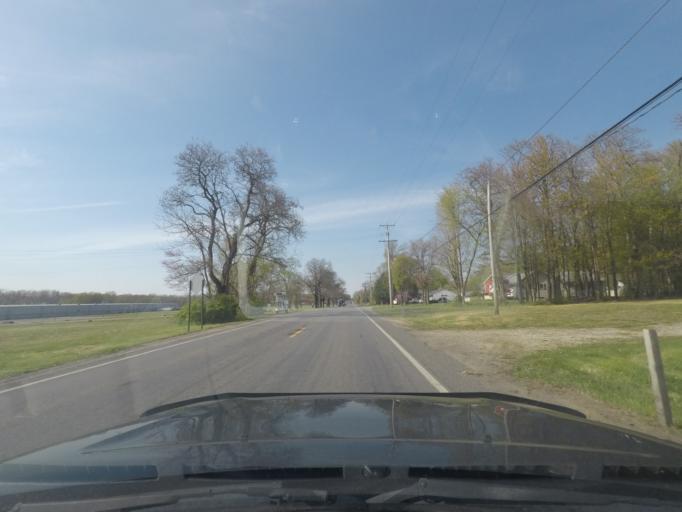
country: US
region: Michigan
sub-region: Berrien County
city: Niles
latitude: 41.7909
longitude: -86.2547
